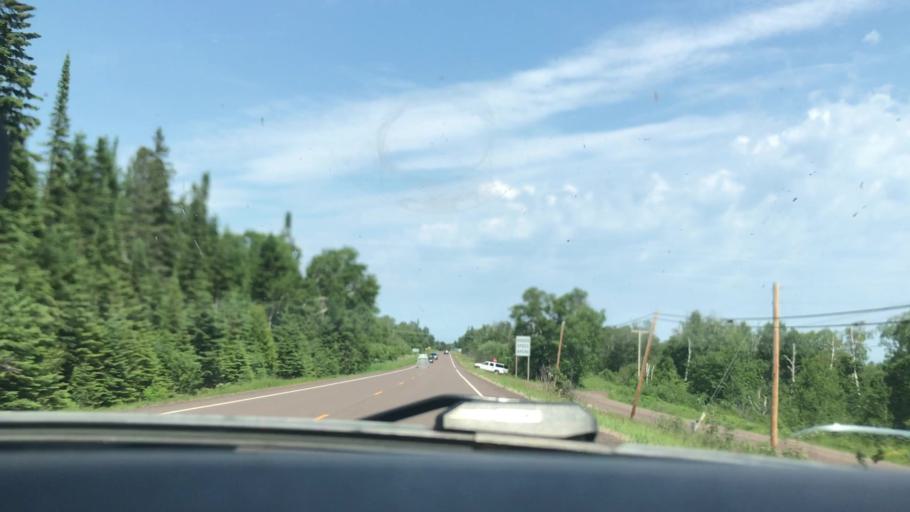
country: US
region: Minnesota
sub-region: Cook County
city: Grand Marais
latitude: 47.6440
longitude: -90.6871
